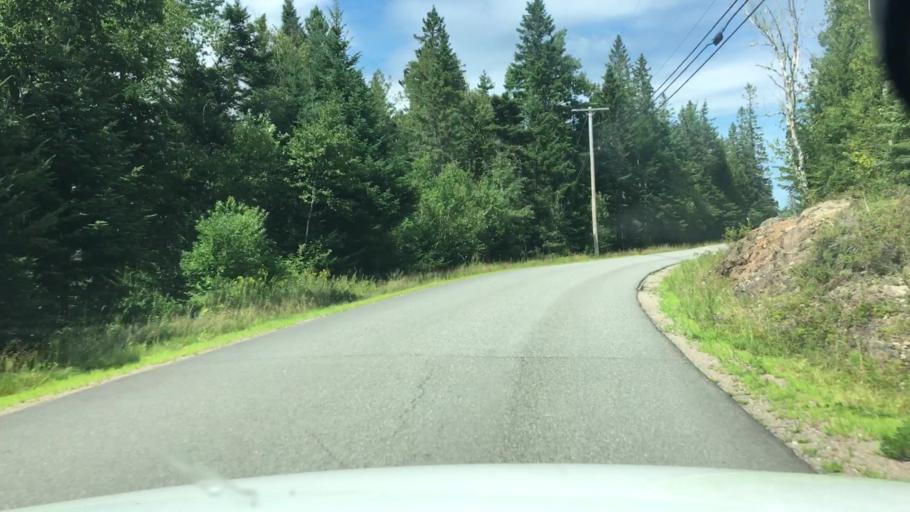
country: CA
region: New Brunswick
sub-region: Charlotte County
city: Saint Andrews
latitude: 44.9798
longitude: -67.0681
